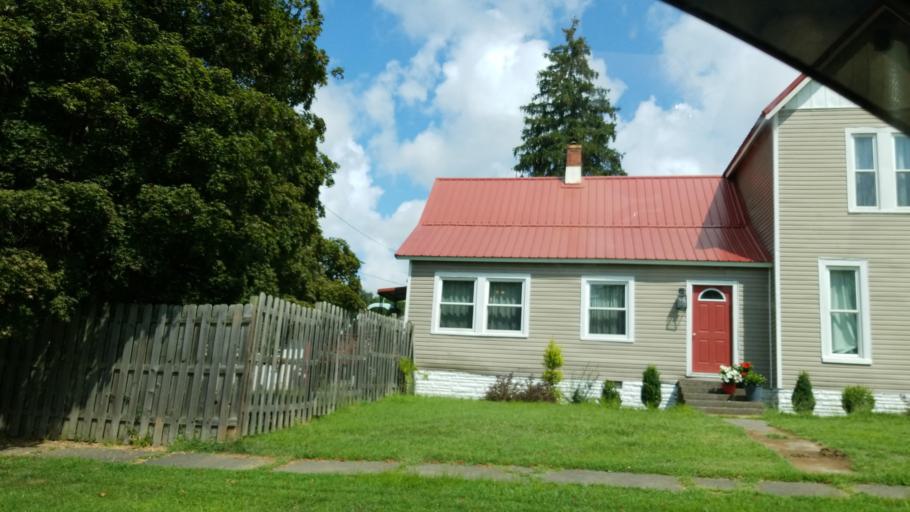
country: US
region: Illinois
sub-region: Saline County
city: Eldorado
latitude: 37.8162
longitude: -88.4388
